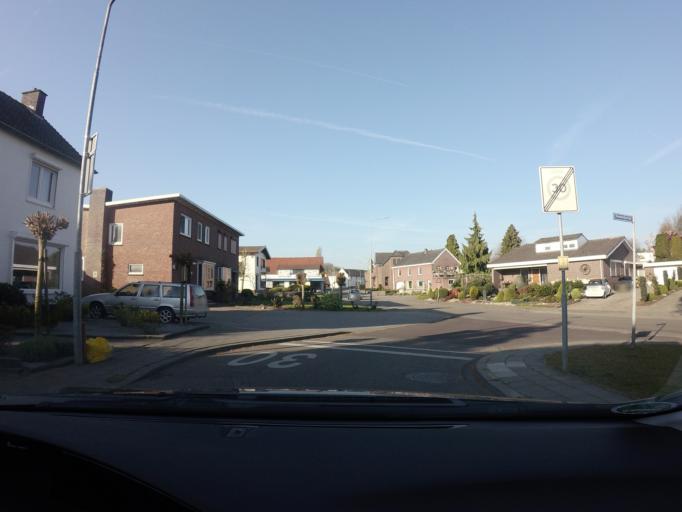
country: NL
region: Limburg
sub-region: Valkenburg aan de Geul
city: Broekhem
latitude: 50.9104
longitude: 5.8275
